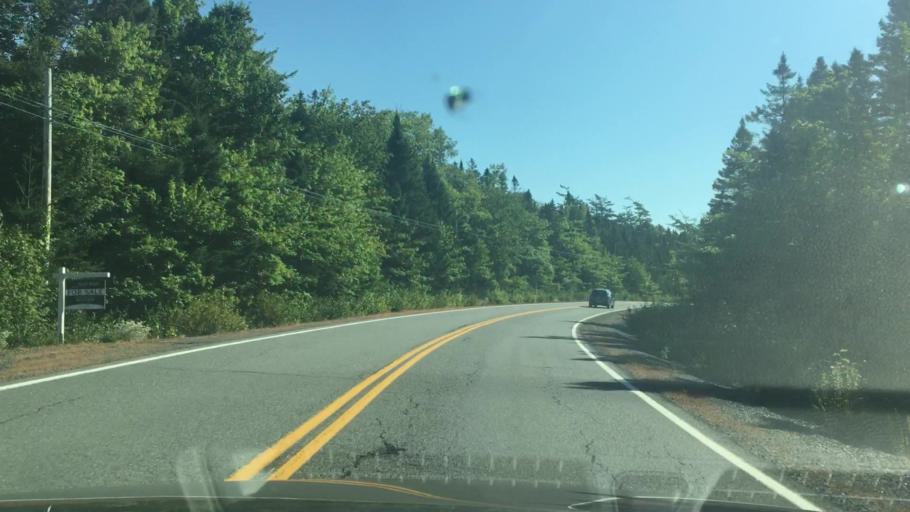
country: CA
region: Nova Scotia
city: Cole Harbour
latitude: 44.8166
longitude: -62.8823
